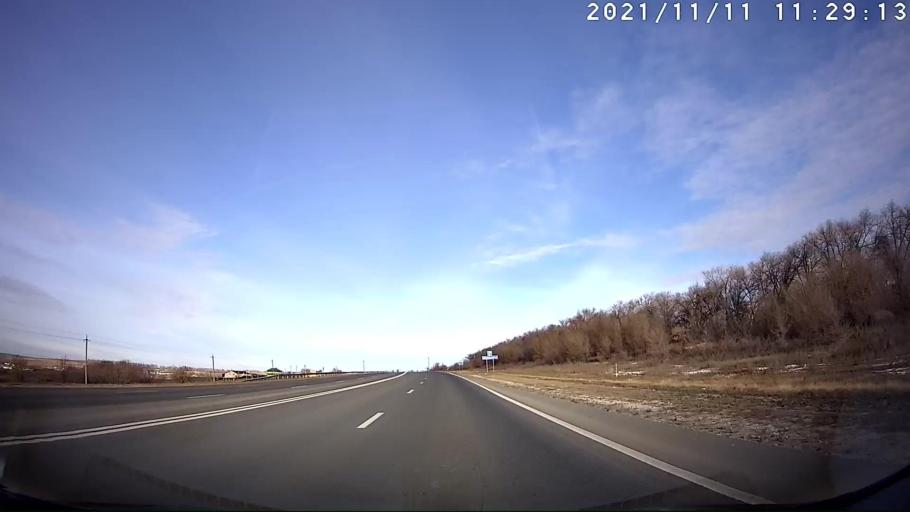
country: RU
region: Samara
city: Varlamovo
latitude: 53.2713
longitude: 48.4798
